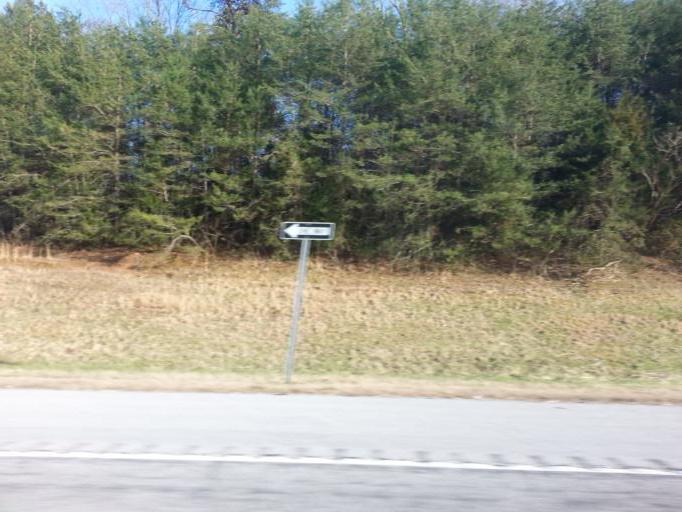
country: US
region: Tennessee
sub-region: Van Buren County
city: Spencer
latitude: 35.7733
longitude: -85.6208
